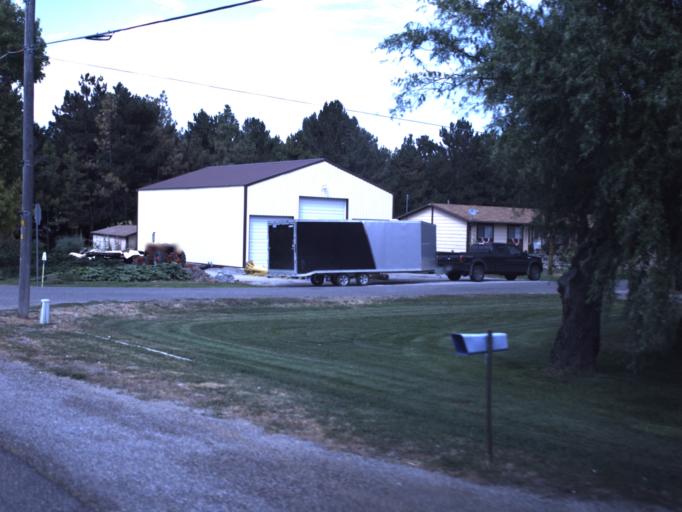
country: US
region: Utah
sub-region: Box Elder County
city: Garland
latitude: 41.8094
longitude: -112.1160
